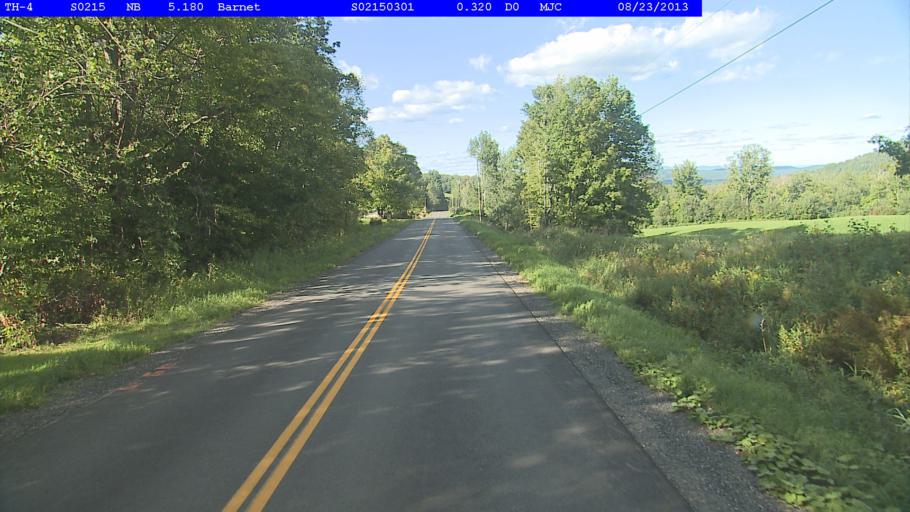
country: US
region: New Hampshire
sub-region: Grafton County
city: Woodsville
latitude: 44.2788
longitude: -72.1729
